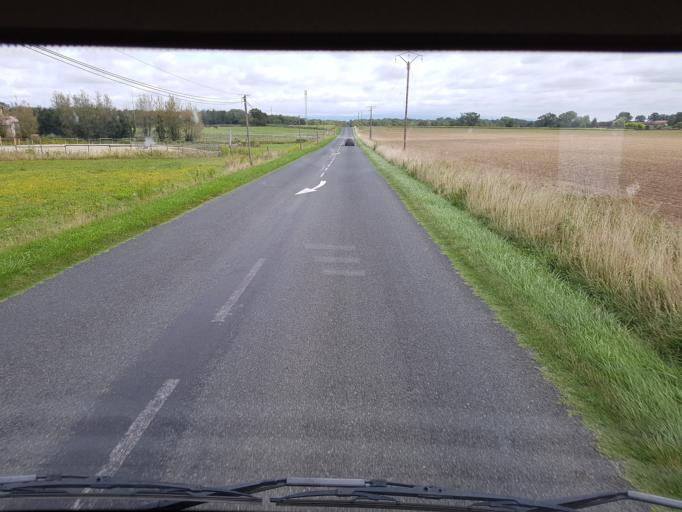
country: FR
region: Rhone-Alpes
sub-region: Departement de l'Ain
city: Beligneux
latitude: 45.9285
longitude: 5.0948
